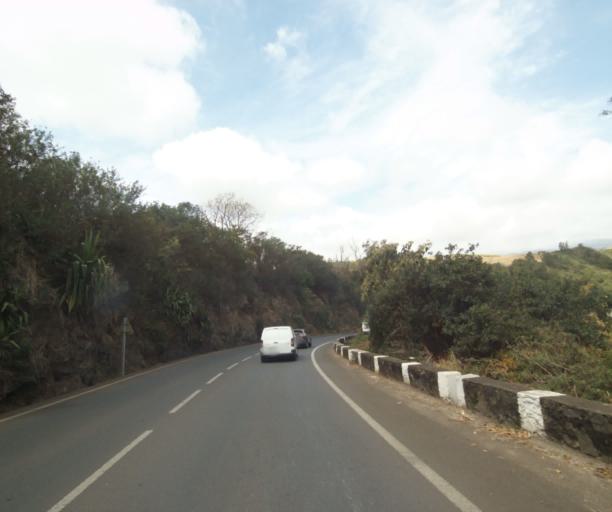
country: RE
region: Reunion
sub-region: Reunion
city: Trois-Bassins
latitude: -21.0691
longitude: 55.2674
